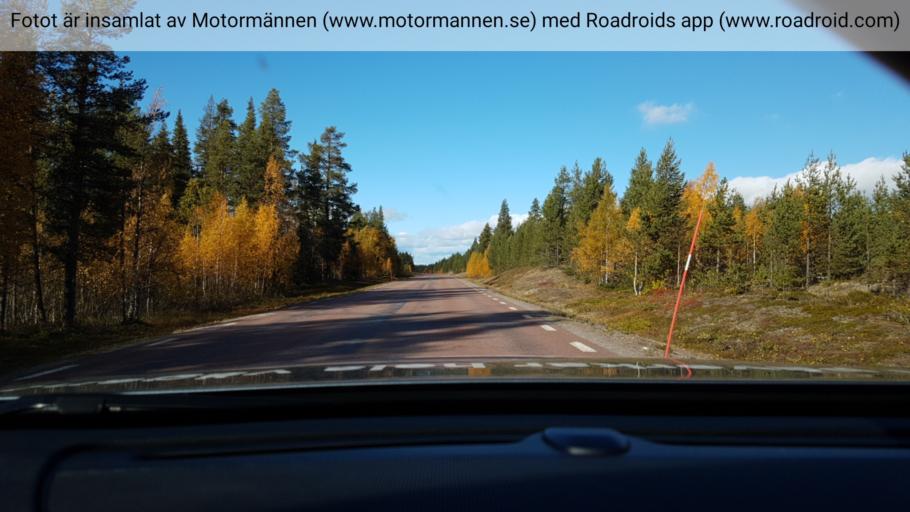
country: SE
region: Norrbotten
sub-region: Arjeplogs Kommun
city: Arjeplog
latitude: 65.9924
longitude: 18.1778
